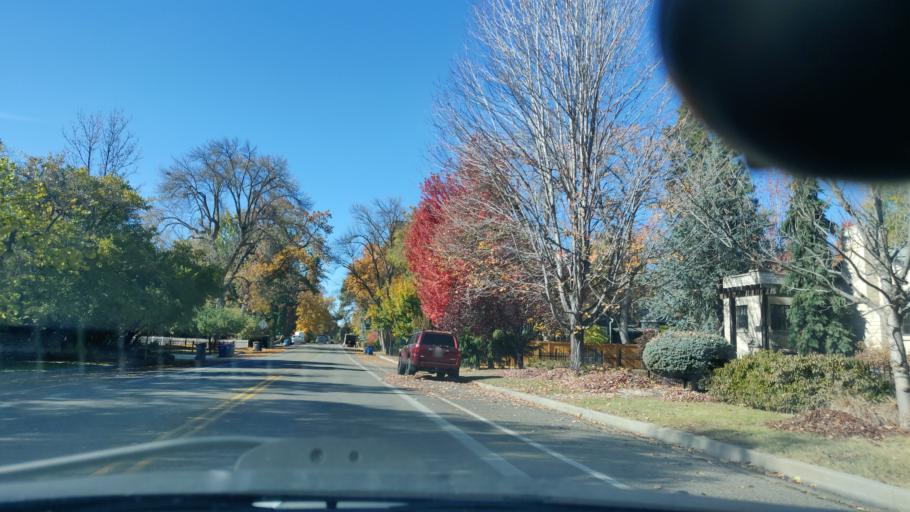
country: US
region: Idaho
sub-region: Ada County
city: Boise
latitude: 43.5935
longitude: -116.2187
